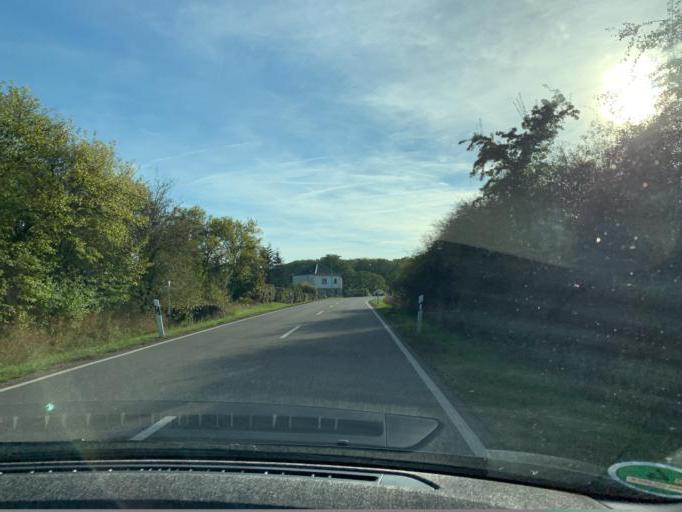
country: DE
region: North Rhine-Westphalia
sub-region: Regierungsbezirk Koln
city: Nideggen
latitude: 50.6842
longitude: 6.5243
